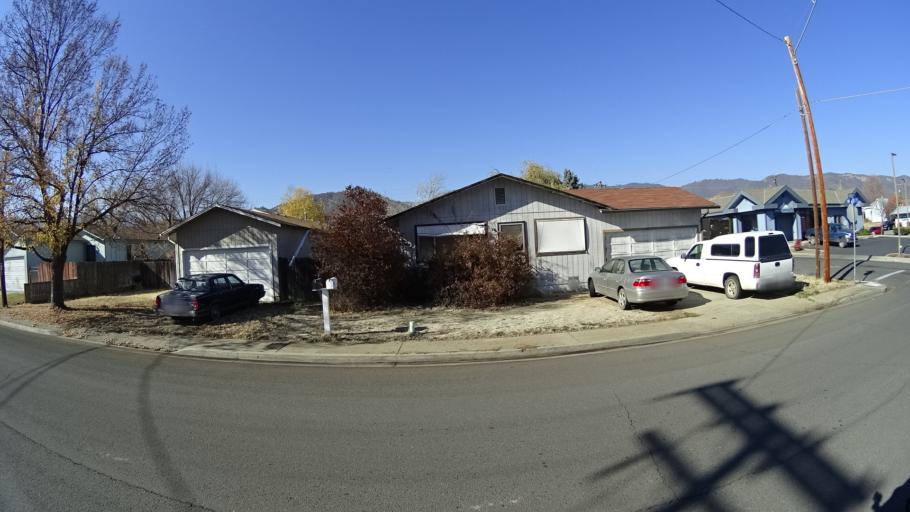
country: US
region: California
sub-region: Siskiyou County
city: Yreka
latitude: 41.7243
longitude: -122.6403
